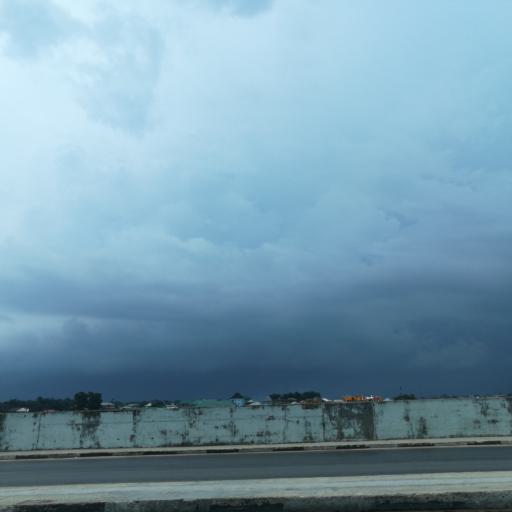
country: NG
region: Rivers
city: Port Harcourt
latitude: 4.8034
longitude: 7.0575
